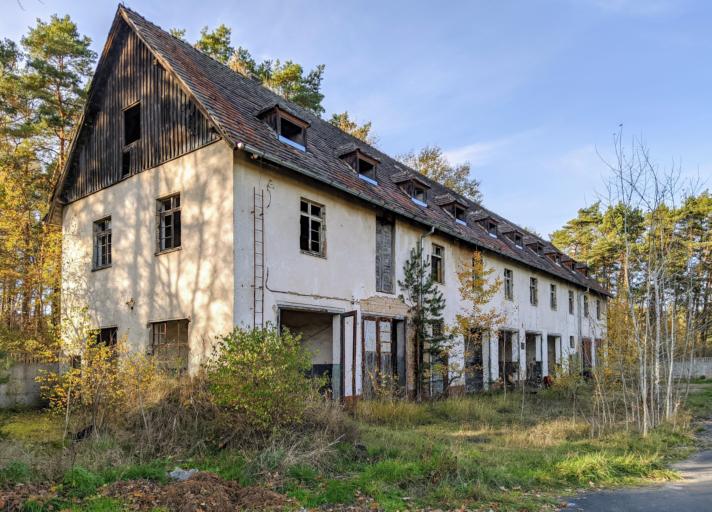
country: PL
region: Lubusz
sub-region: Powiat miedzyrzecki
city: Miedzyrzecz
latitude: 52.4083
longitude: 15.4774
